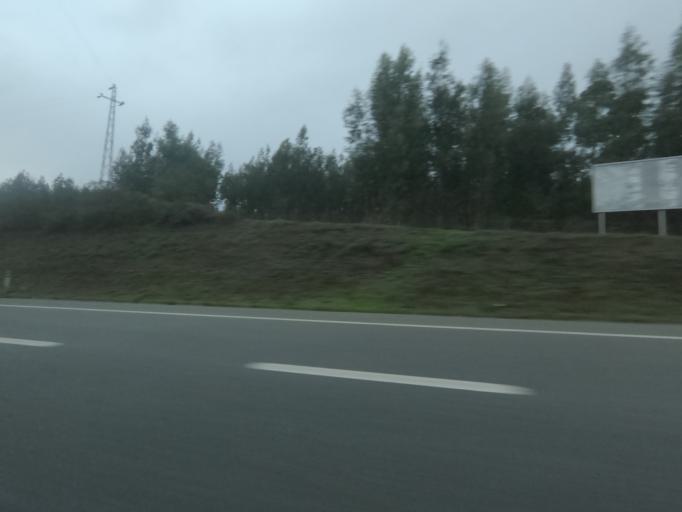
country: PT
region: Braga
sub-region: Barcelos
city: Galegos
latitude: 41.6074
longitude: -8.5497
